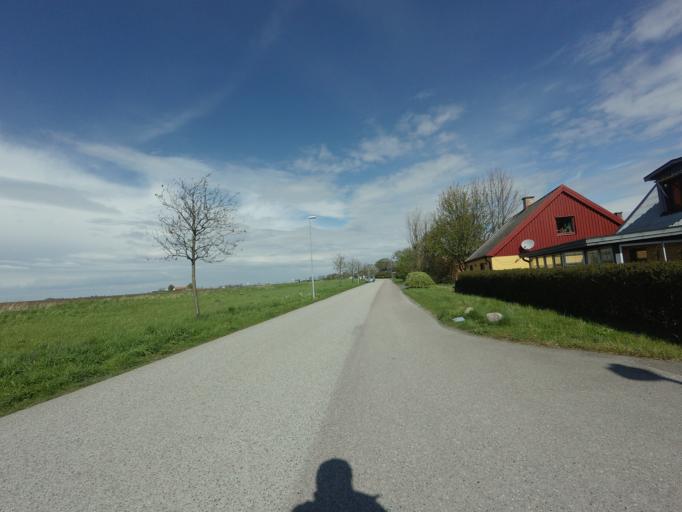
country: SE
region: Skane
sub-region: Vellinge Kommun
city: Vellinge
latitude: 55.4877
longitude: 13.0104
